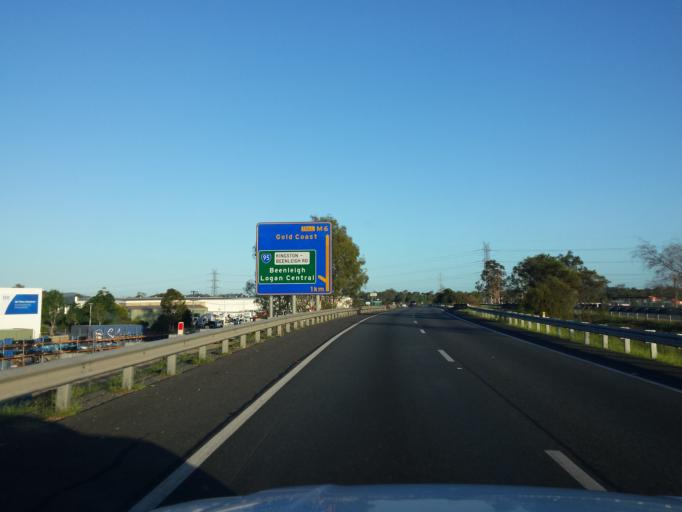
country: AU
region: Queensland
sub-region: Logan
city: Logan City
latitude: -27.6674
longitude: 153.1124
